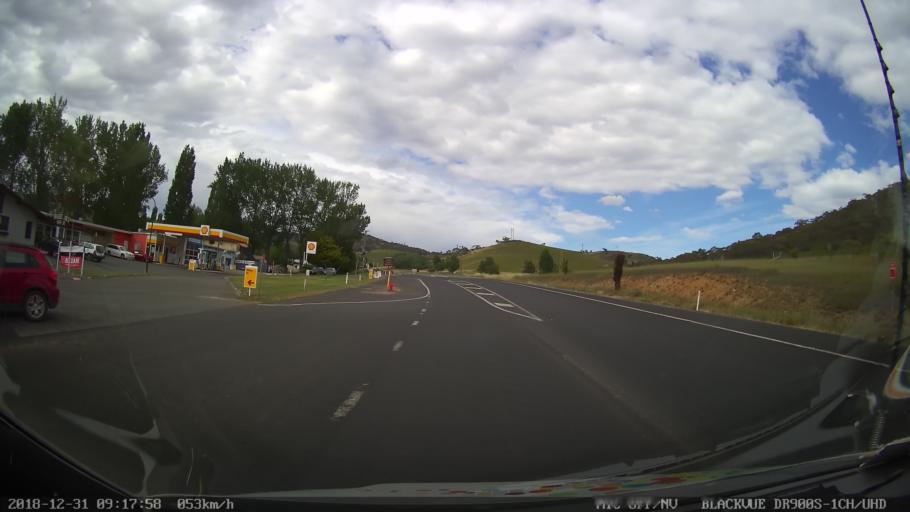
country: AU
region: New South Wales
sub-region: Snowy River
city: Jindabyne
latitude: -36.4095
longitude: 148.5968
